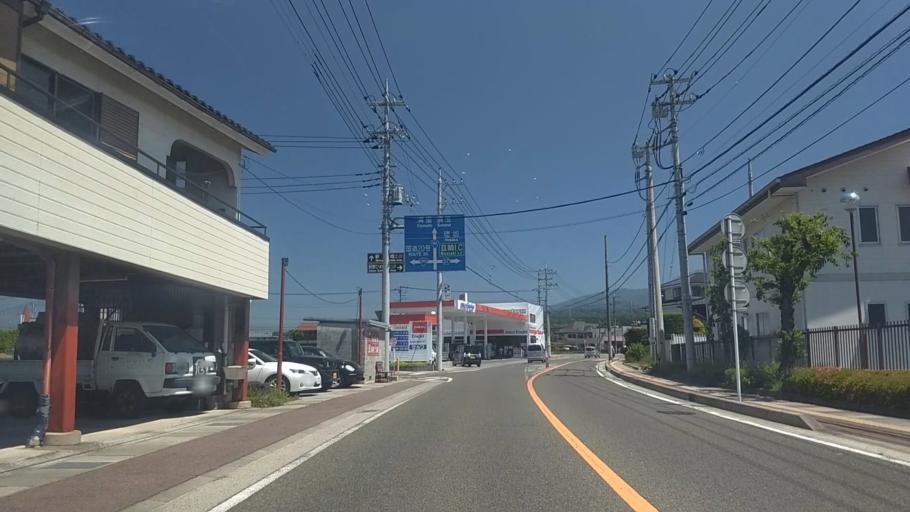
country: JP
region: Yamanashi
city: Nirasaki
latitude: 35.7173
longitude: 138.4487
